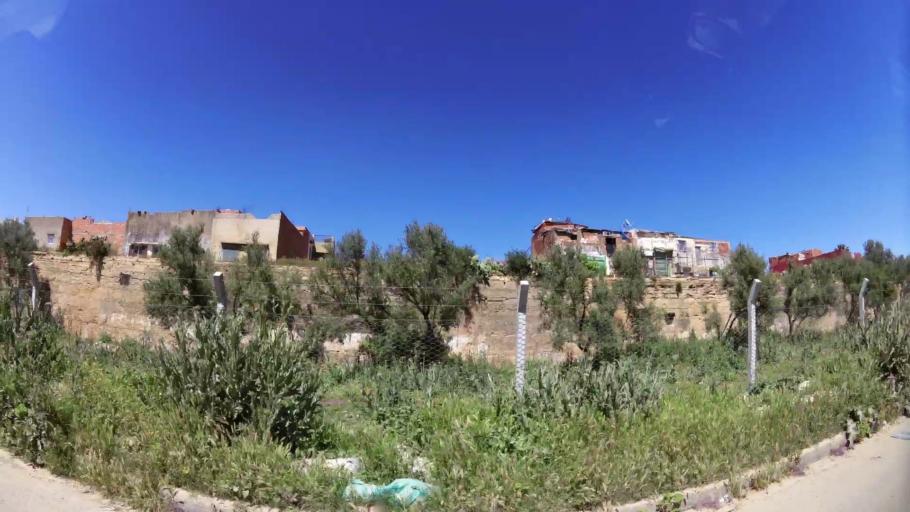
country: MA
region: Meknes-Tafilalet
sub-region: Meknes
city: Meknes
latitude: 33.8624
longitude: -5.5536
